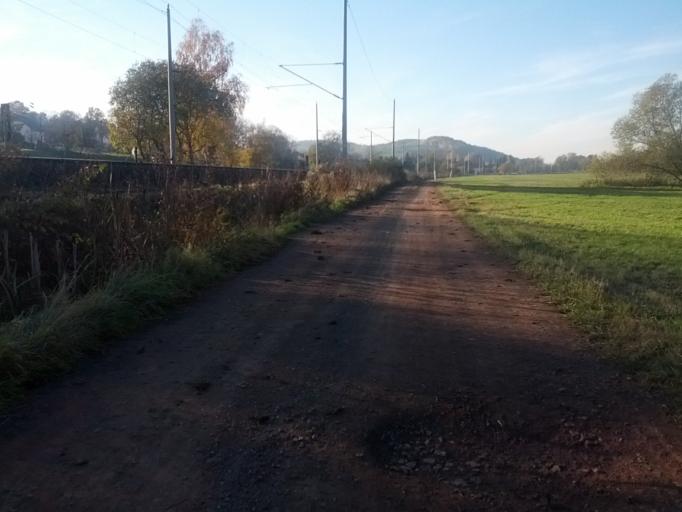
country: DE
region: Thuringia
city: Seebach
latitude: 50.9423
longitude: 10.4407
